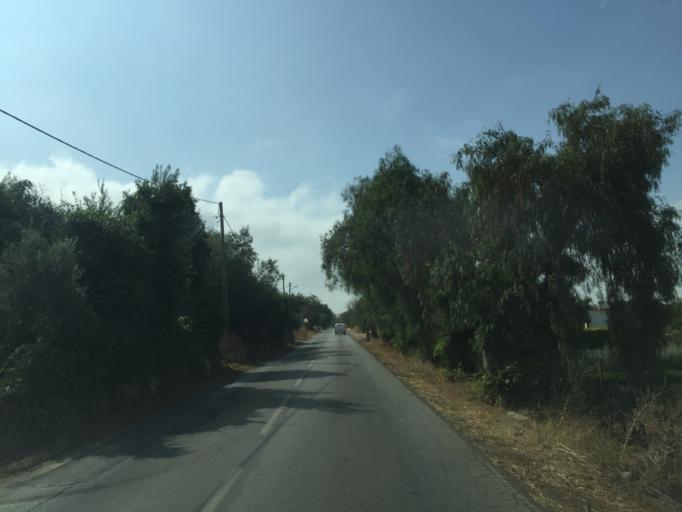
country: PT
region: Faro
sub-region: Sao Bras de Alportel
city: Sao Bras de Alportel
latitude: 37.0847
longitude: -7.8918
